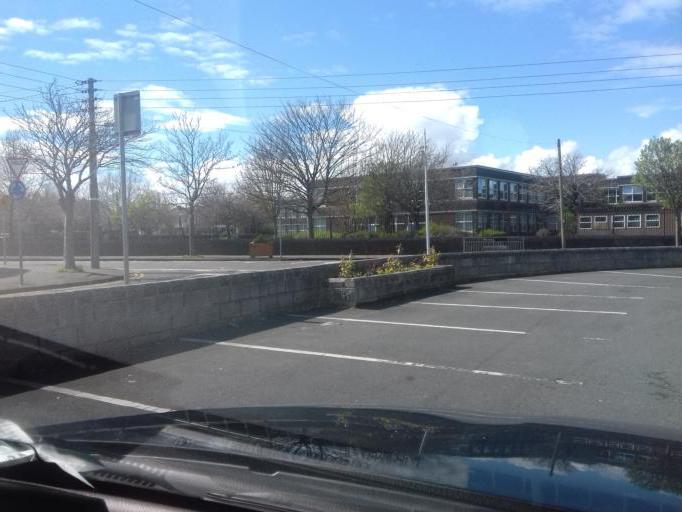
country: IE
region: Leinster
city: Donaghmede
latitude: 53.3886
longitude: -6.1682
